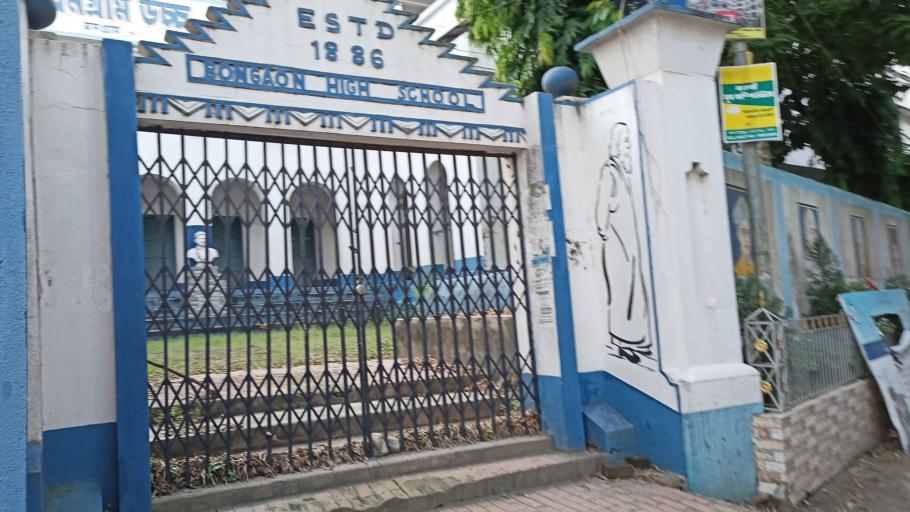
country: IN
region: West Bengal
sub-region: North 24 Parganas
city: Bangaon
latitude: 23.0456
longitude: 88.8281
